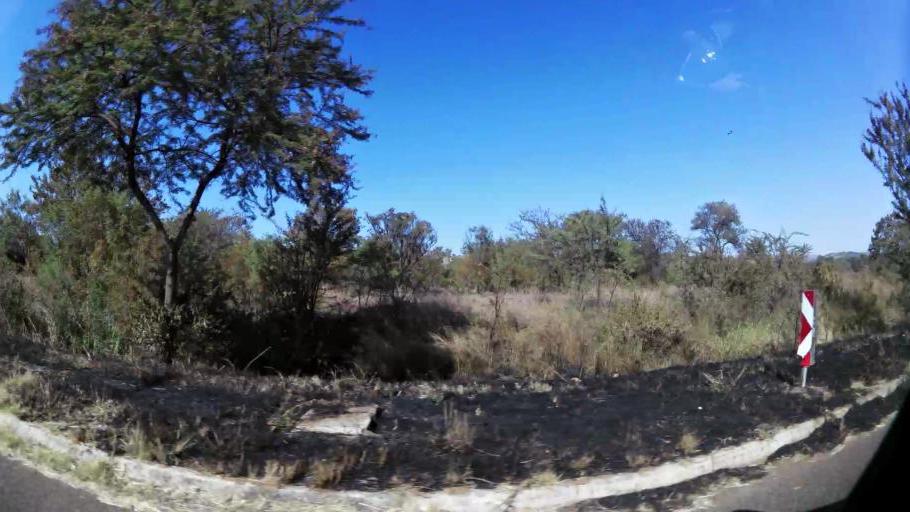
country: ZA
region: North-West
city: Ga-Rankuwa
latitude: -25.6612
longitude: 28.0903
